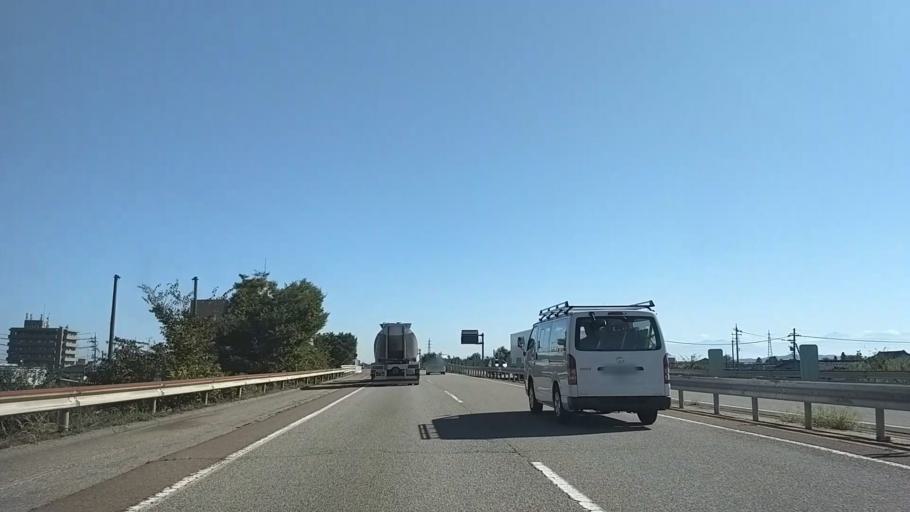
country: JP
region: Toyama
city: Nanto-shi
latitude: 36.6254
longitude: 136.9572
